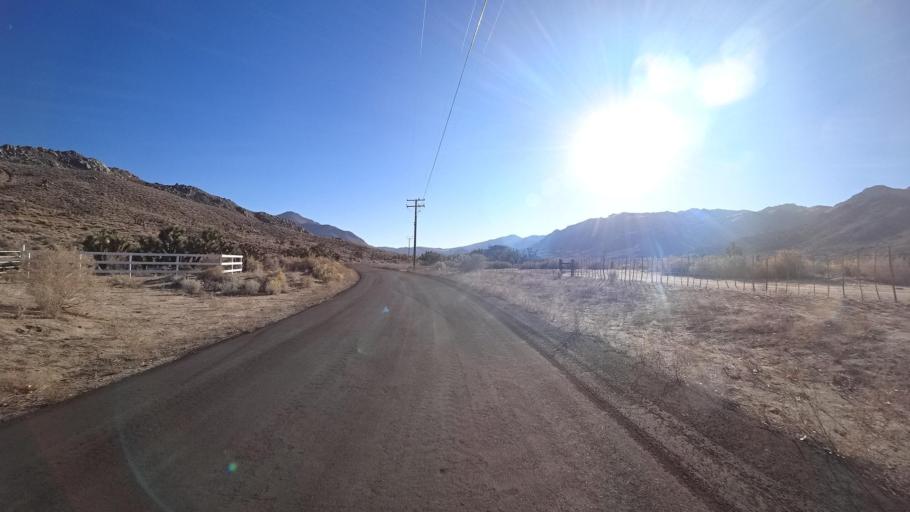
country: US
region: California
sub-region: Kern County
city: Weldon
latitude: 35.5110
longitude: -118.2025
